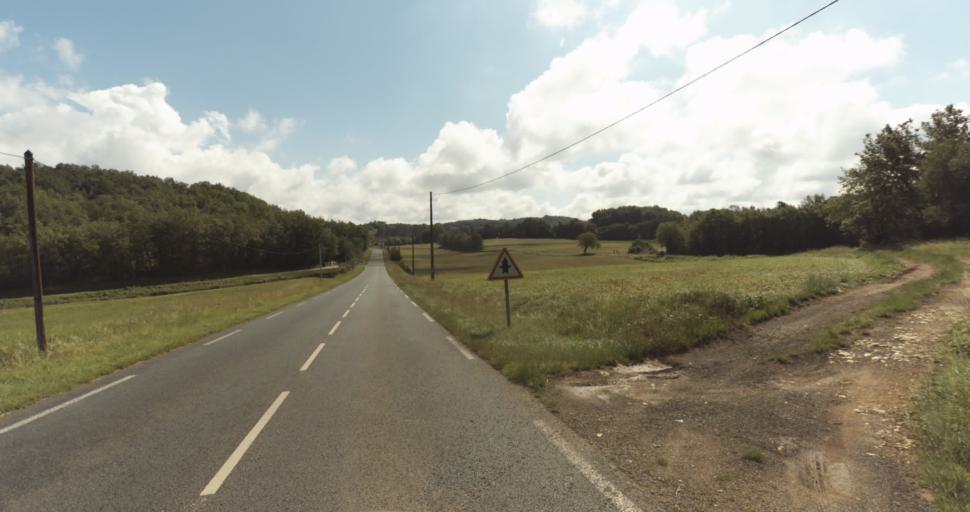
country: FR
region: Aquitaine
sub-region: Departement de la Dordogne
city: Beaumont-du-Perigord
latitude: 44.8444
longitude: 0.8353
